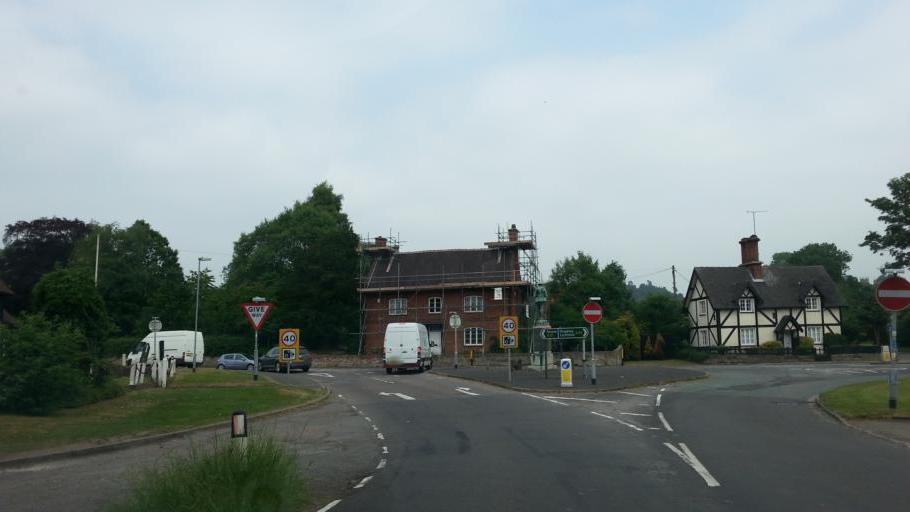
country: GB
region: England
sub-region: Staffordshire
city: Stafford
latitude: 52.8611
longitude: -2.0787
